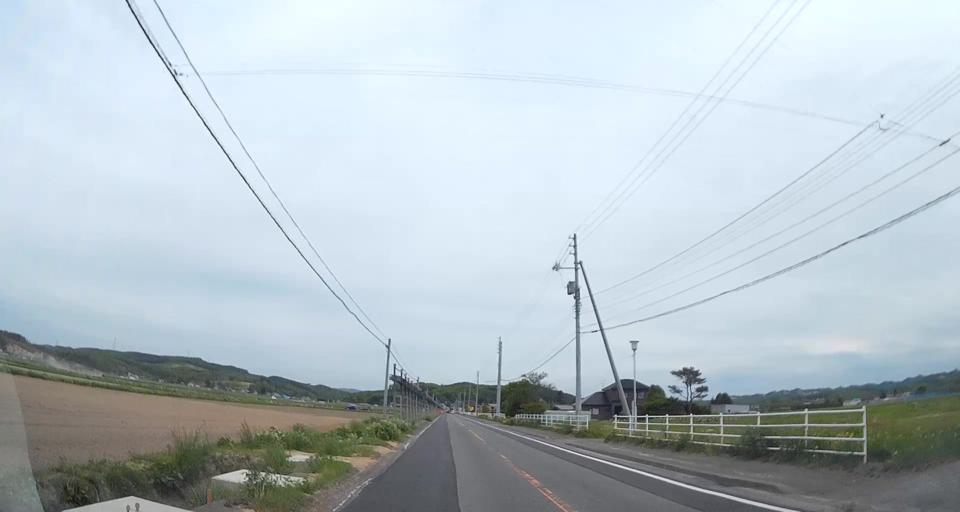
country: JP
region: Hokkaido
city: Chitose
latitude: 42.7305
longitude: 141.8852
